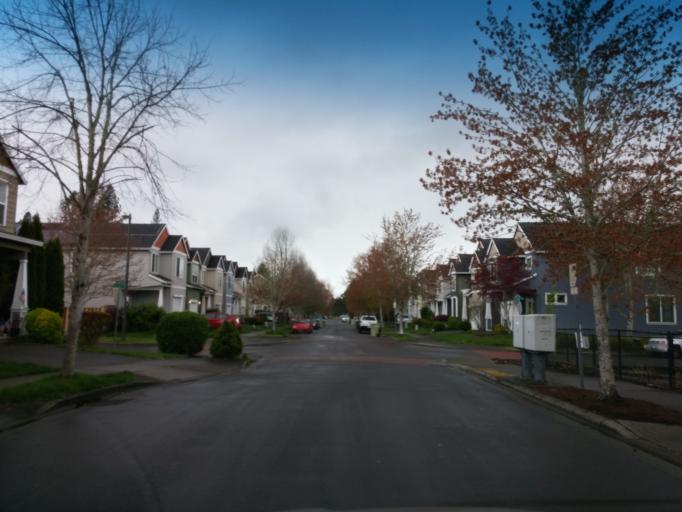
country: US
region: Oregon
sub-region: Washington County
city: Aloha
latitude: 45.5115
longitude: -122.8577
